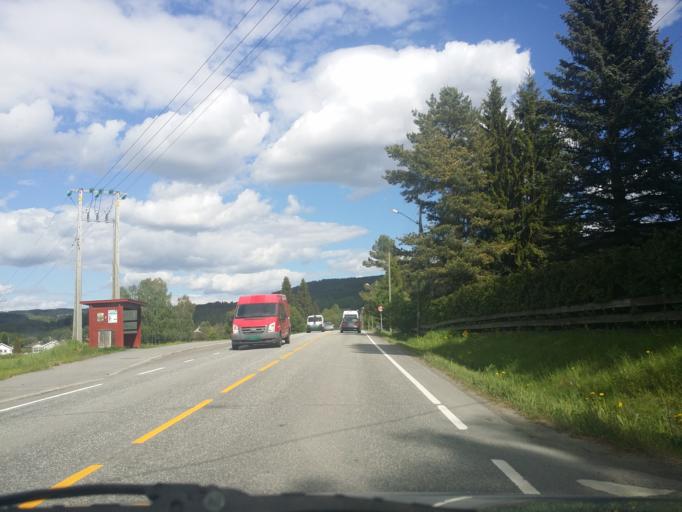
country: NO
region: Oppland
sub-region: Jevnaker
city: Jevnaker
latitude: 60.2410
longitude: 10.4123
